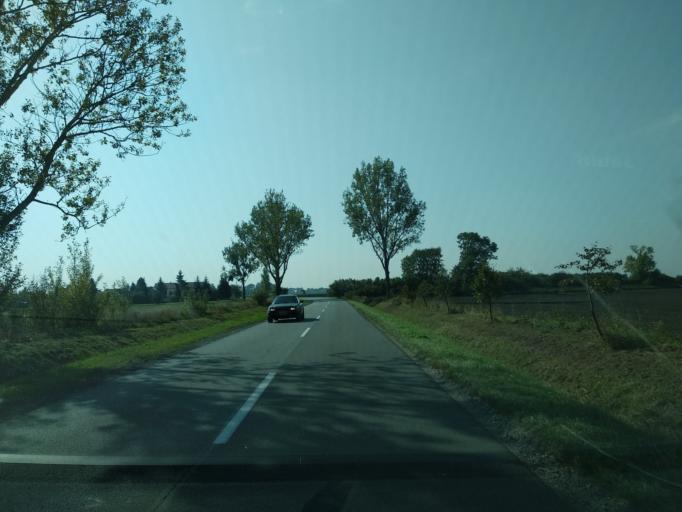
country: PL
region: Lower Silesian Voivodeship
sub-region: Powiat wroclawski
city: Zerniki Wroclawskie
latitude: 51.0377
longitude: 17.0298
